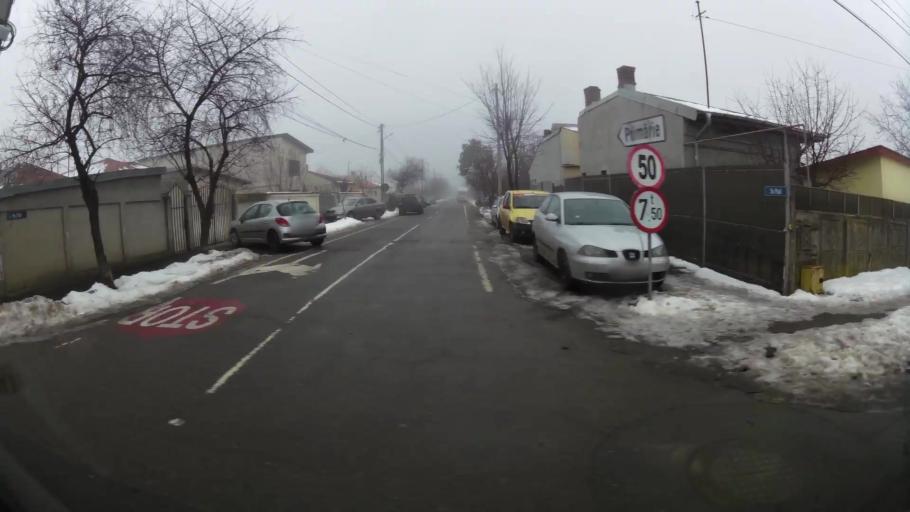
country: RO
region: Ilfov
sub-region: Comuna Chiajna
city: Chiajna
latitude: 44.4621
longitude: 25.9827
